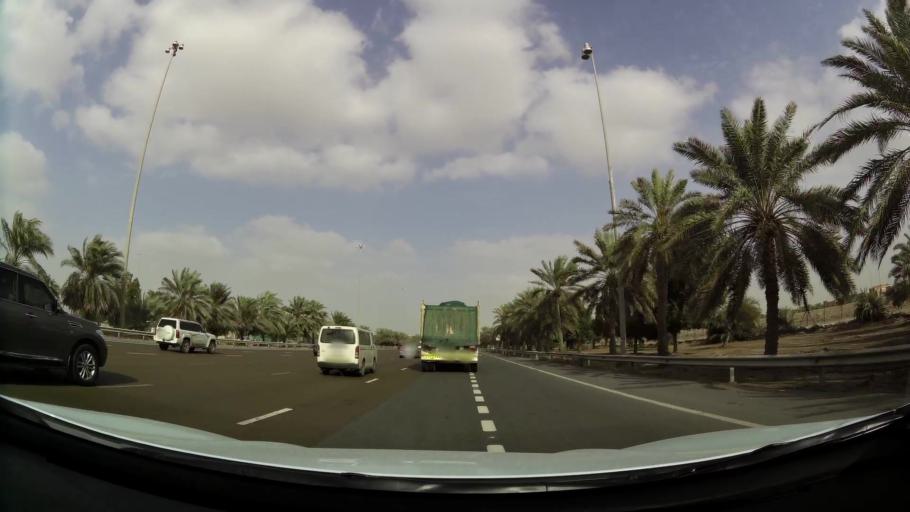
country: AE
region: Abu Dhabi
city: Abu Dhabi
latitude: 24.4250
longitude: 54.5299
